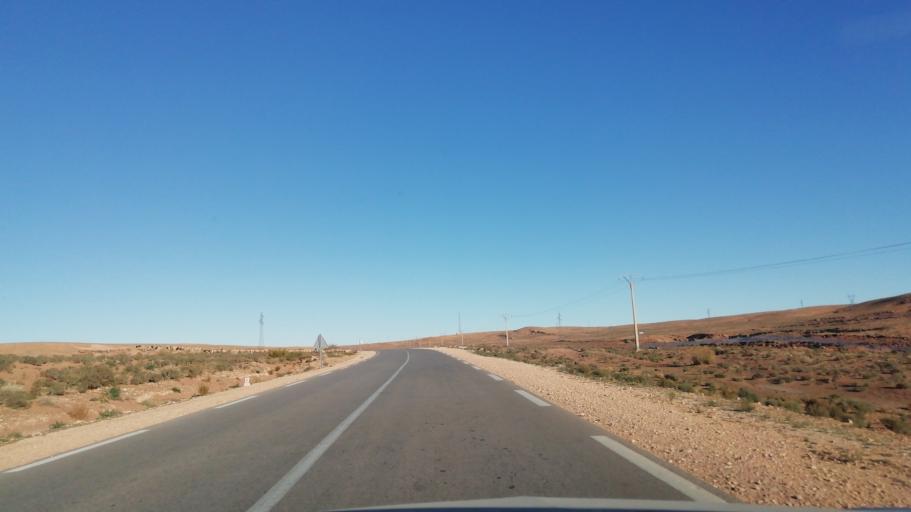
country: DZ
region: El Bayadh
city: El Abiodh Sidi Cheikh
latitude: 33.1690
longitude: 0.4293
